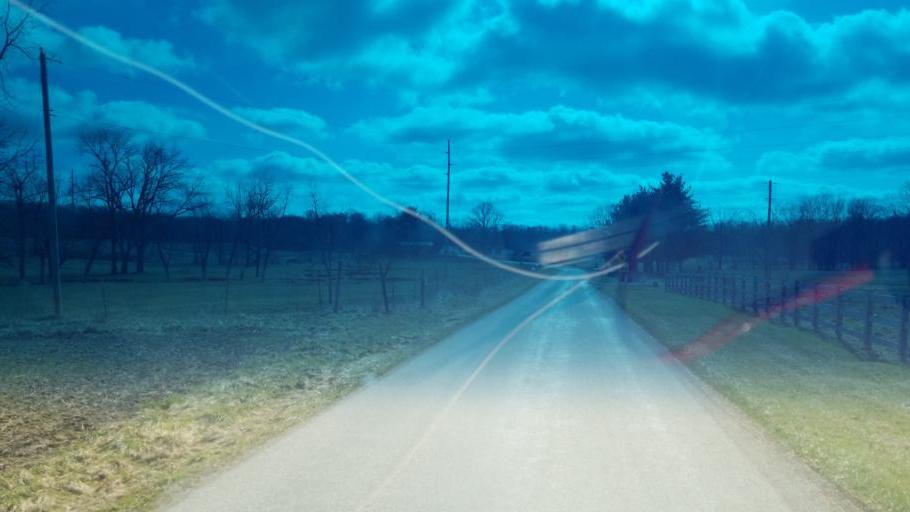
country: US
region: Ohio
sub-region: Crawford County
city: Galion
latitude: 40.6647
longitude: -82.7060
